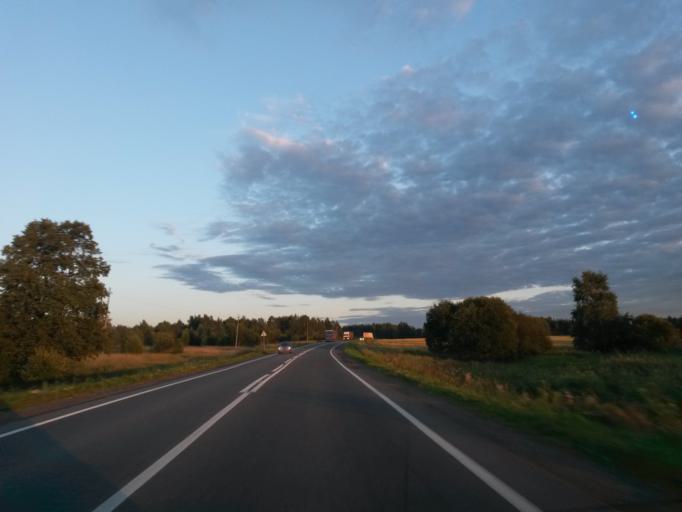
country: RU
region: Jaroslavl
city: Gavrilov-Yam
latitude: 57.3219
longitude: 39.9309
